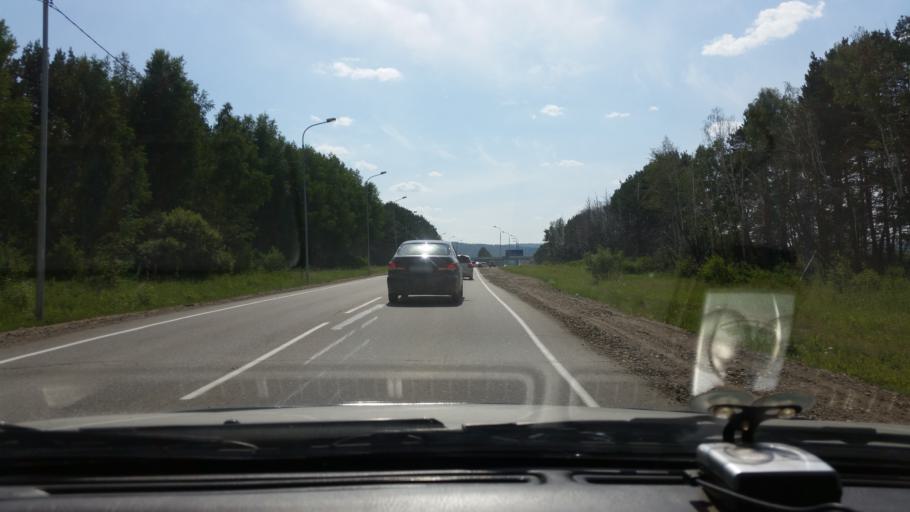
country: RU
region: Irkutsk
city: Baklashi
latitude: 52.1860
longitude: 104.0166
